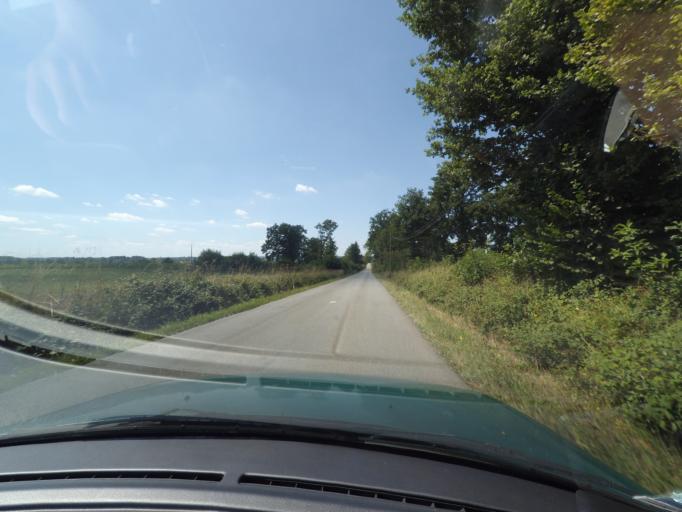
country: FR
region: Limousin
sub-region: Departement de la Haute-Vienne
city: Aixe-sur-Vienne
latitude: 45.7827
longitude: 1.1624
